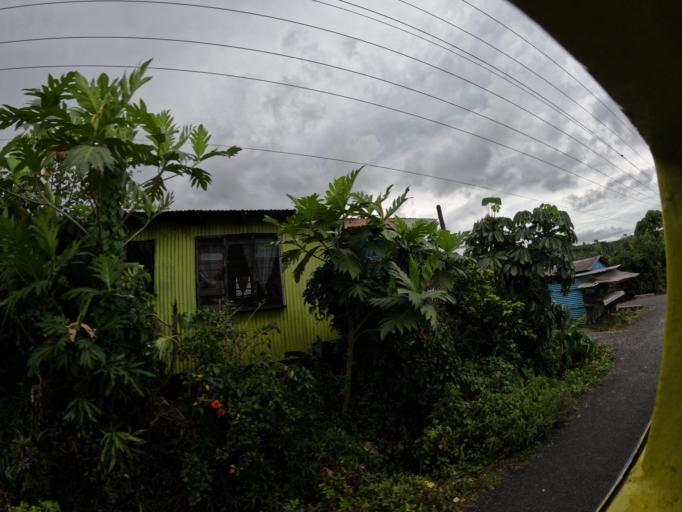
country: FJ
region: Central
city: Suva
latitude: -18.0746
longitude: 178.4602
